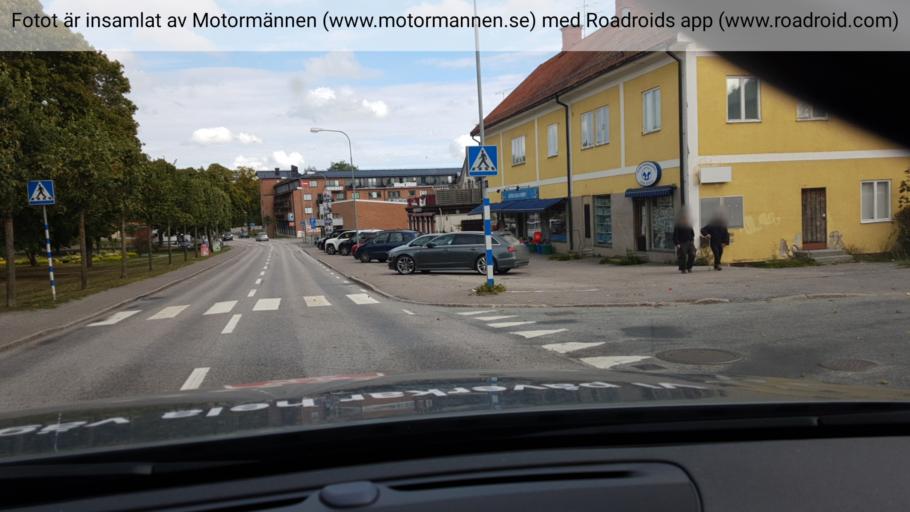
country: SE
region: Stockholm
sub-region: Norrtalje Kommun
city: Rimbo
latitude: 59.7430
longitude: 18.3645
